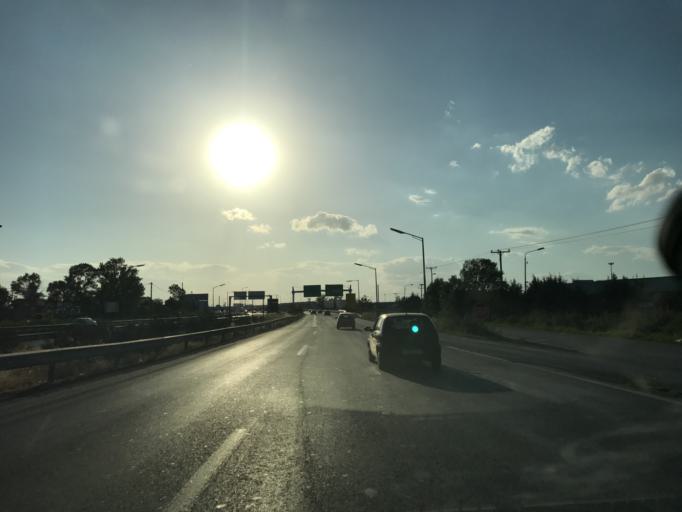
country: GR
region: Central Macedonia
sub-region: Nomos Thessalonikis
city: Menemeni
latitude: 40.6548
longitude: 22.8947
